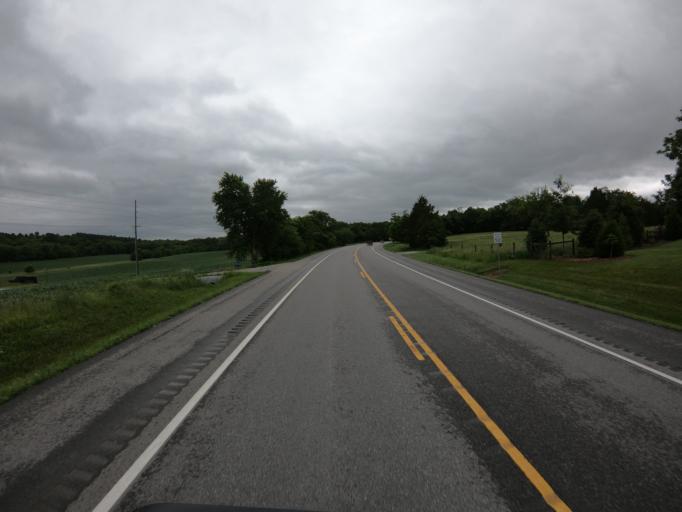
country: US
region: Maryland
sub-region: Washington County
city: Keedysville
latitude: 39.4892
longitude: -77.7022
